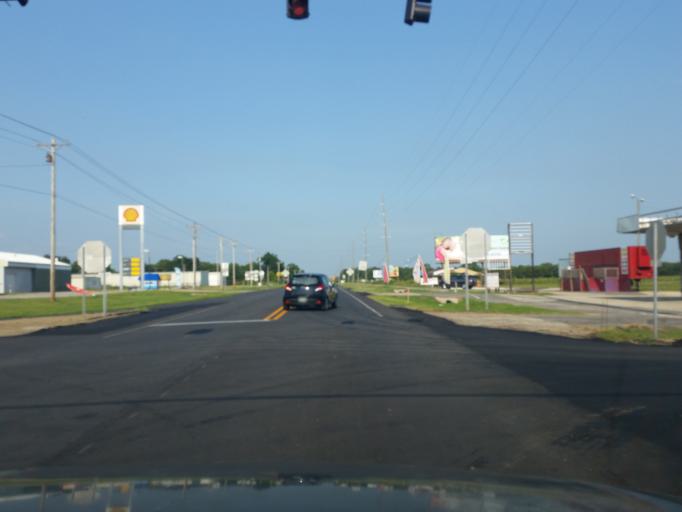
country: US
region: Alabama
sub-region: Baldwin County
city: Point Clear
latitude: 30.4212
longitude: -87.8863
